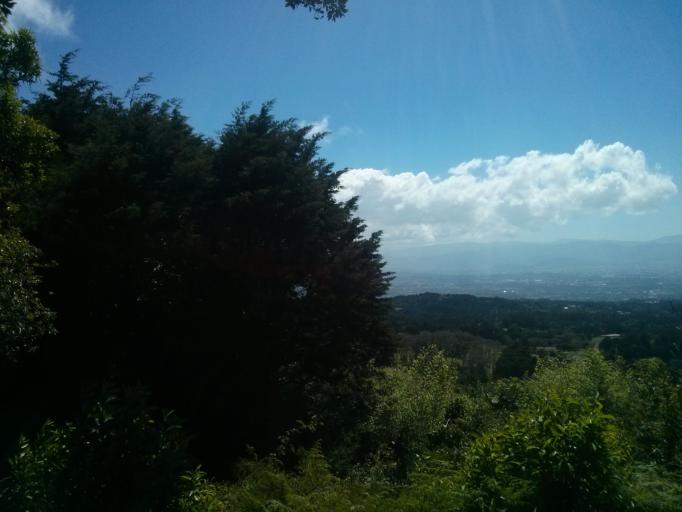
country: CR
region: Heredia
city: San Josecito
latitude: 10.0657
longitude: -84.0768
